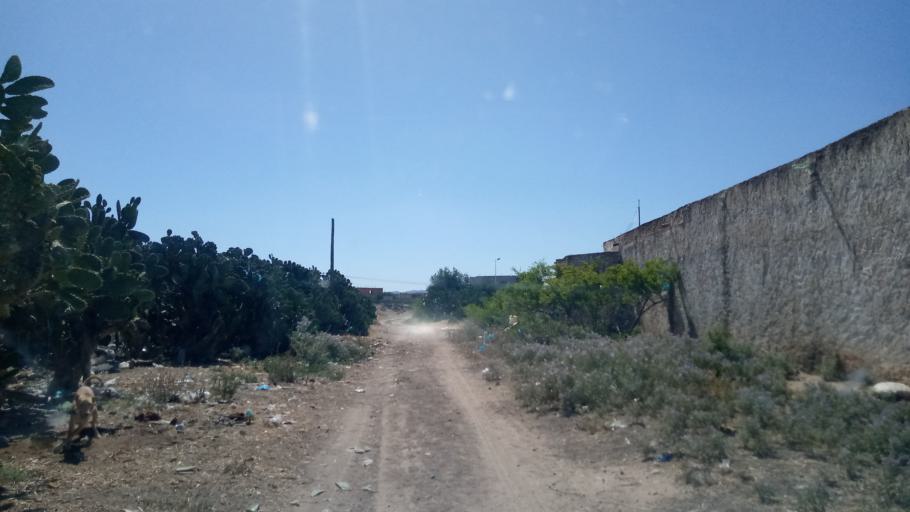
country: TN
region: Al Qayrawan
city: Sbikha
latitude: 36.1299
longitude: 10.0908
